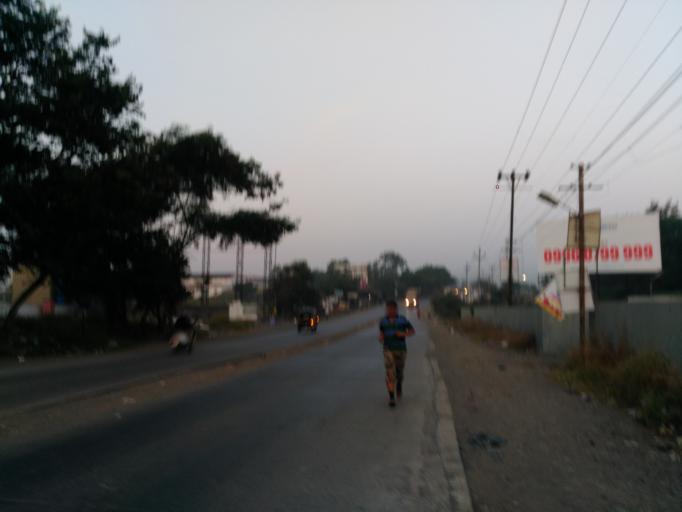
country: IN
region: Maharashtra
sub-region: Pune Division
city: Pune
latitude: 18.4513
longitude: 73.8954
